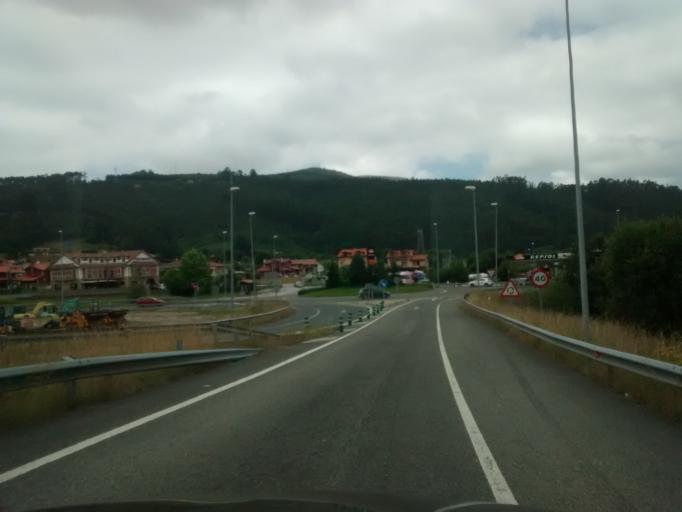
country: ES
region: Cantabria
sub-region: Provincia de Cantabria
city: Luzmela
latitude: 43.3270
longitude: -4.1907
